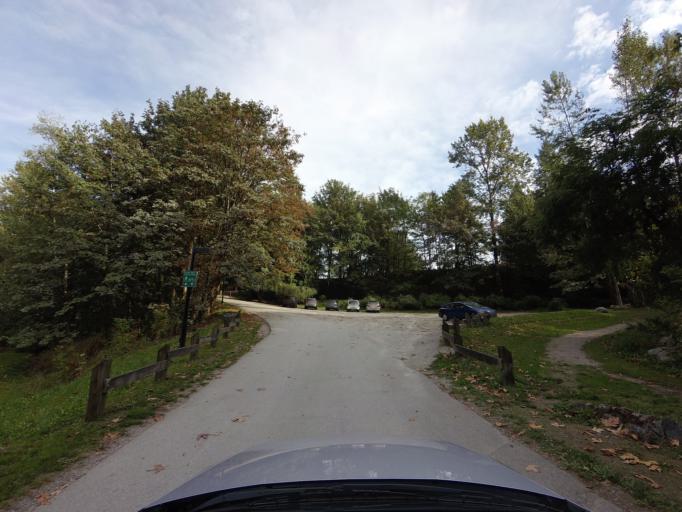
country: CA
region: British Columbia
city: New Westminster
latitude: 49.2352
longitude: -122.8913
